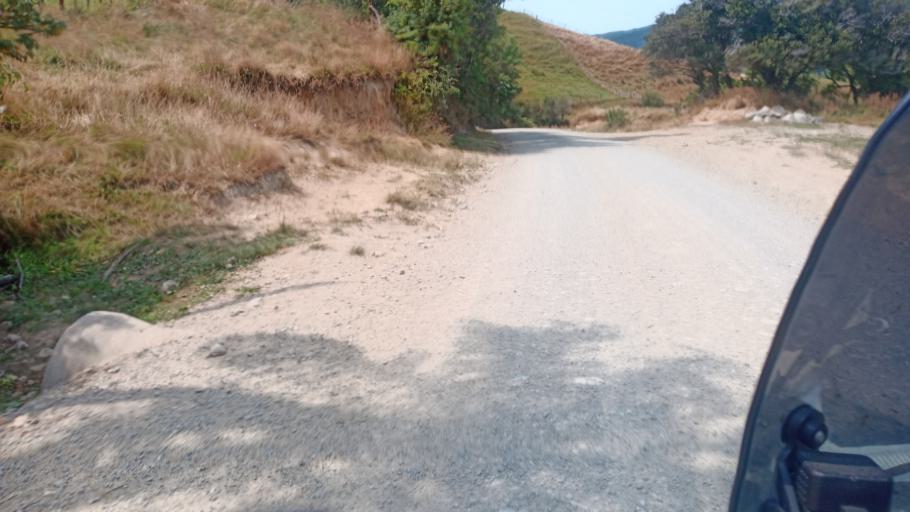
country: NZ
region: Bay of Plenty
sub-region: Opotiki District
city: Opotiki
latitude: -37.6579
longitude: 178.1294
